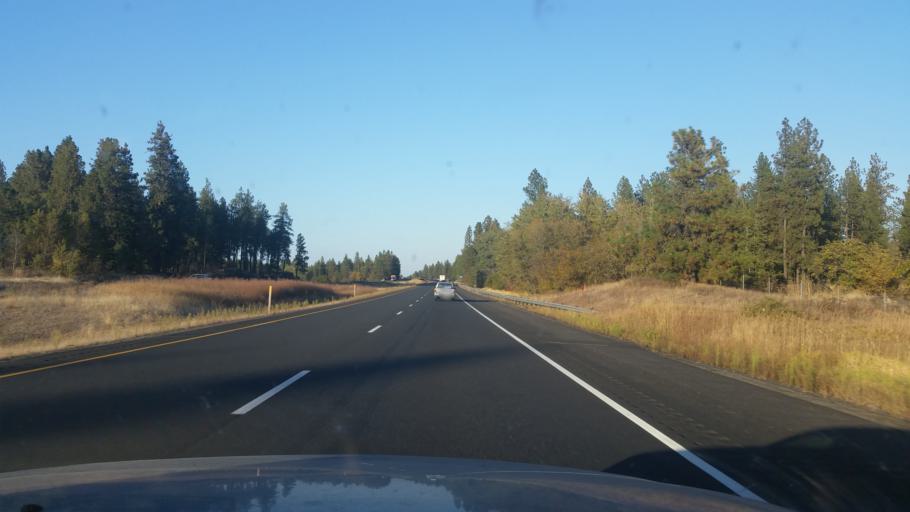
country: US
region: Washington
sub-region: Spokane County
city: Medical Lake
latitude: 47.5089
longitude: -117.6836
